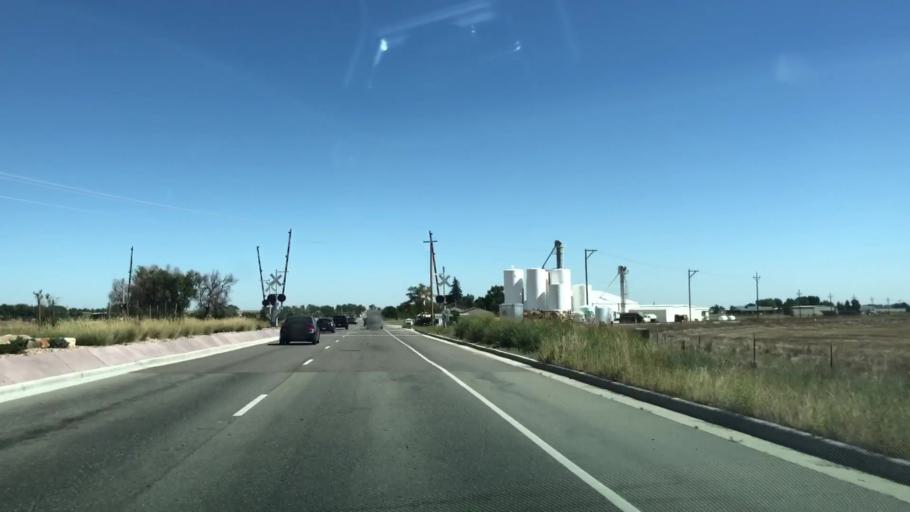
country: US
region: Colorado
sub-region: Weld County
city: Windsor
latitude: 40.5228
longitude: -104.9735
